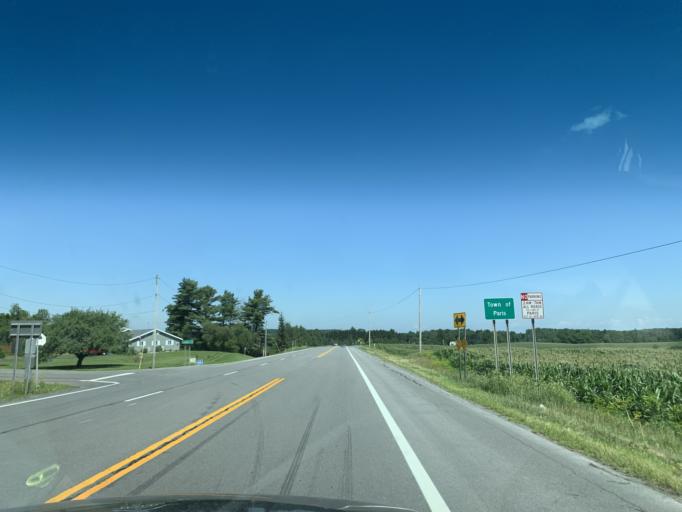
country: US
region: New York
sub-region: Oneida County
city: Chadwicks
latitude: 42.9376
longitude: -75.2513
